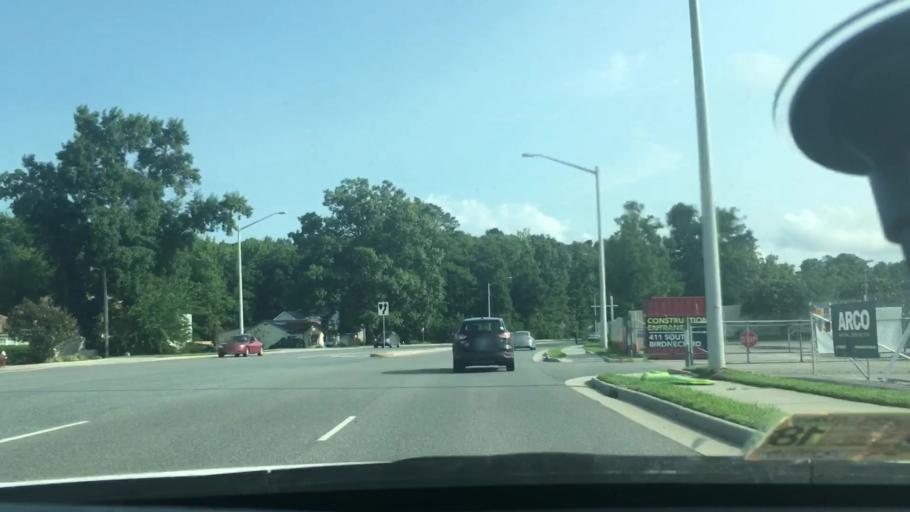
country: US
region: Virginia
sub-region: City of Virginia Beach
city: Virginia Beach
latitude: 36.8291
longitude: -75.9973
